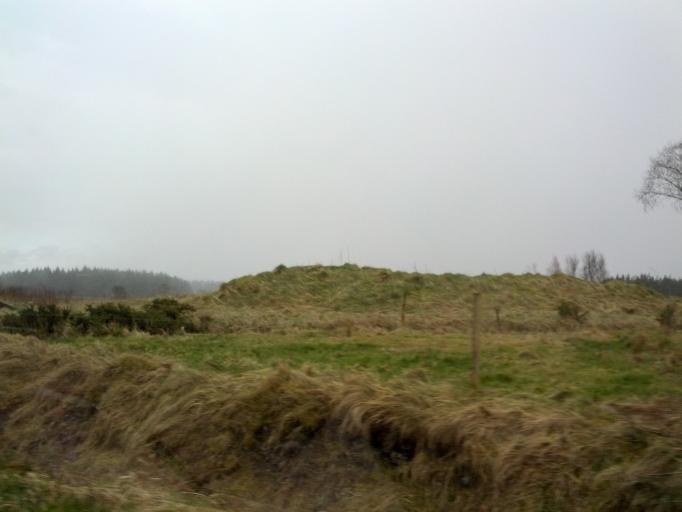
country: IE
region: Connaught
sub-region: County Galway
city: Athenry
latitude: 53.4057
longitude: -8.5987
